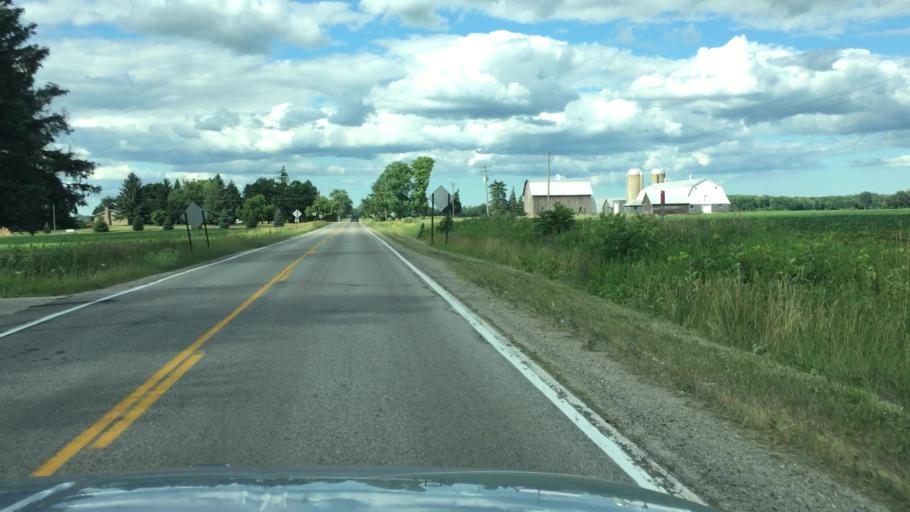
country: US
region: Michigan
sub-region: Saint Clair County
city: Capac
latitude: 43.0660
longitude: -82.9290
